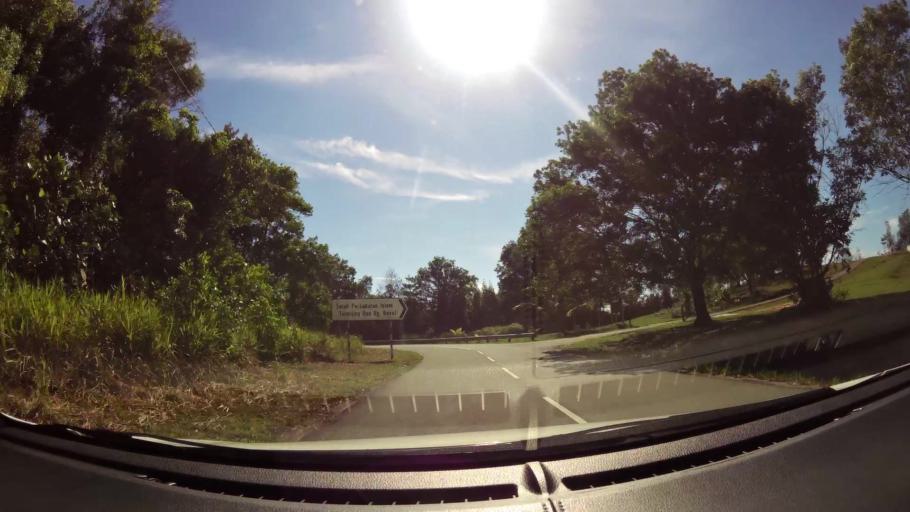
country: BN
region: Brunei and Muara
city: Bandar Seri Begawan
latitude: 4.9682
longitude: 114.9356
